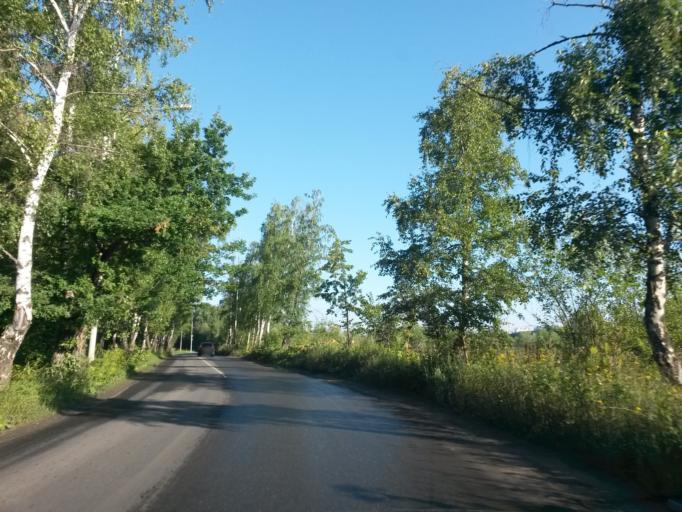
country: RU
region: Moskovskaya
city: Shcherbinka
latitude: 55.5066
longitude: 37.5951
